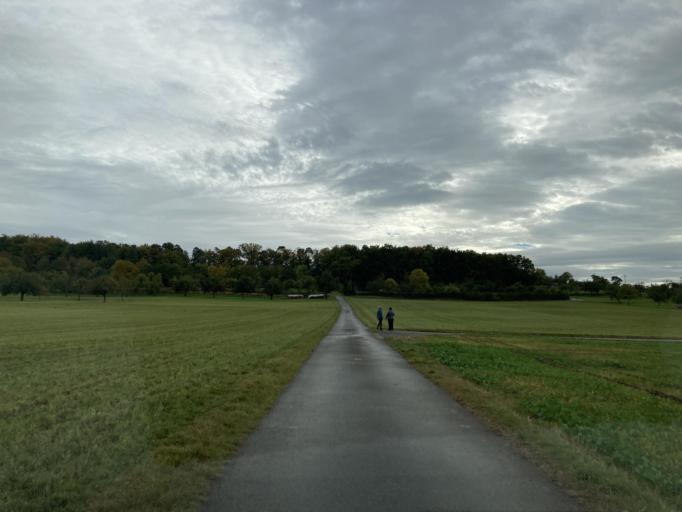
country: DE
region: Baden-Wuerttemberg
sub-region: Regierungsbezirk Stuttgart
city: Bondorf
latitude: 48.5208
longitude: 8.8644
